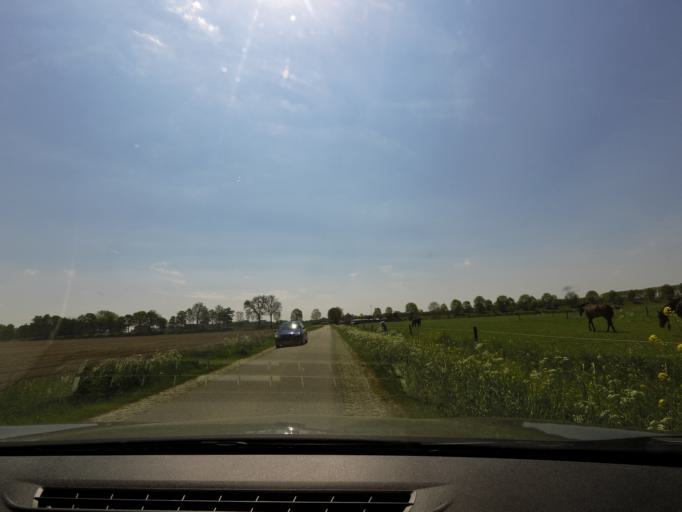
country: NL
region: South Holland
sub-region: Gemeente Binnenmaas
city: Heinenoord
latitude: 51.8479
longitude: 4.4615
